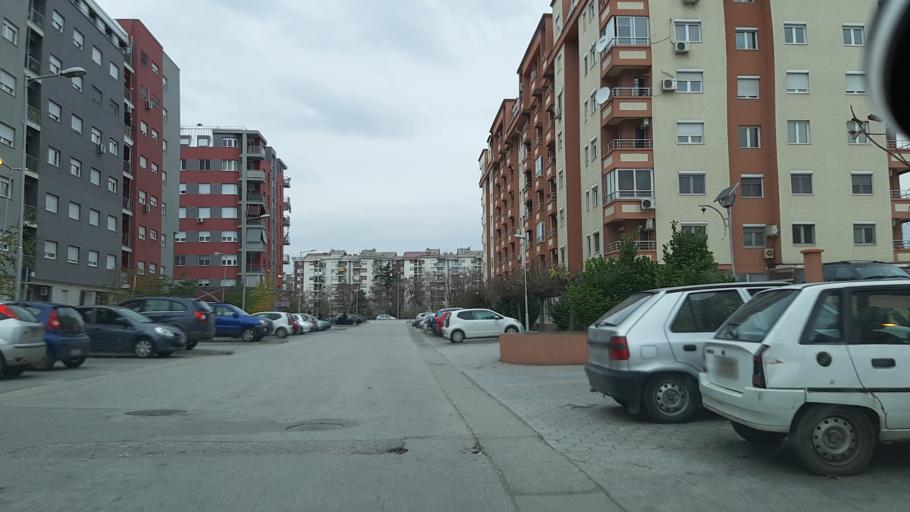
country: MK
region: Kisela Voda
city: Usje
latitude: 41.9808
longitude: 21.4717
